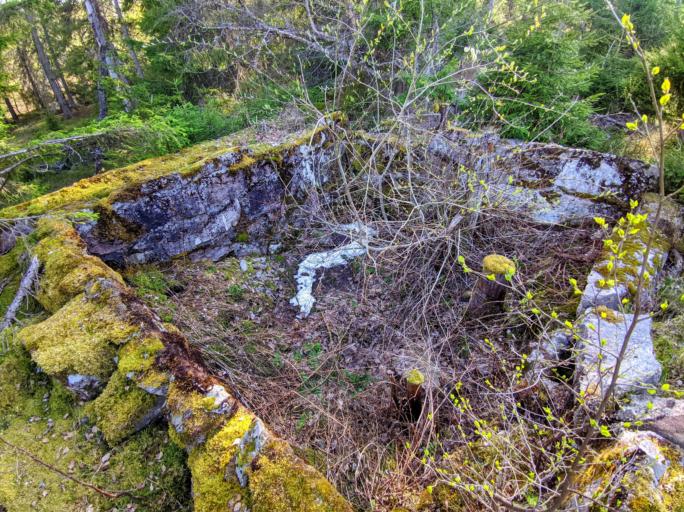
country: NO
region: Akershus
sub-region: Nittedal
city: Aneby
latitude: 60.1760
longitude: 10.8719
